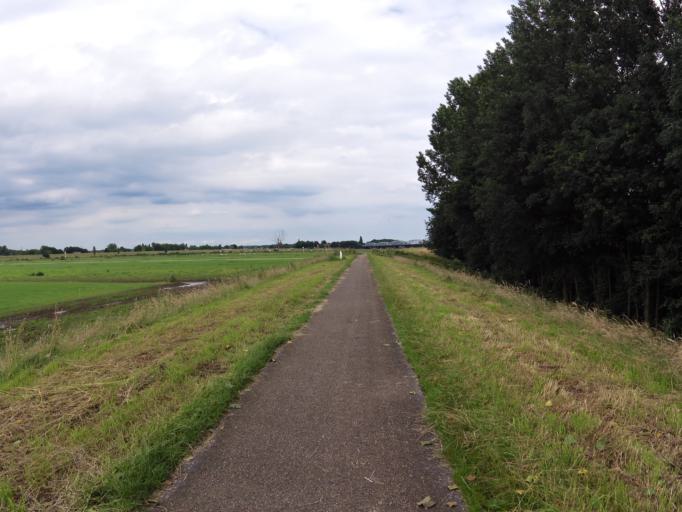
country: NL
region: North Brabant
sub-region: Gemeente Grave
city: Grave
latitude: 51.7702
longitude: 5.7238
